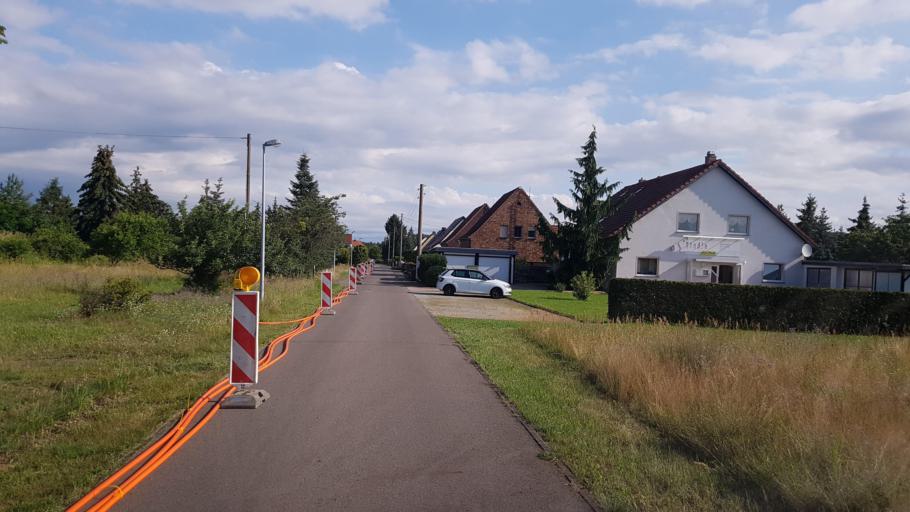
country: DE
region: Brandenburg
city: Grossraschen
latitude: 51.5853
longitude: 14.0192
